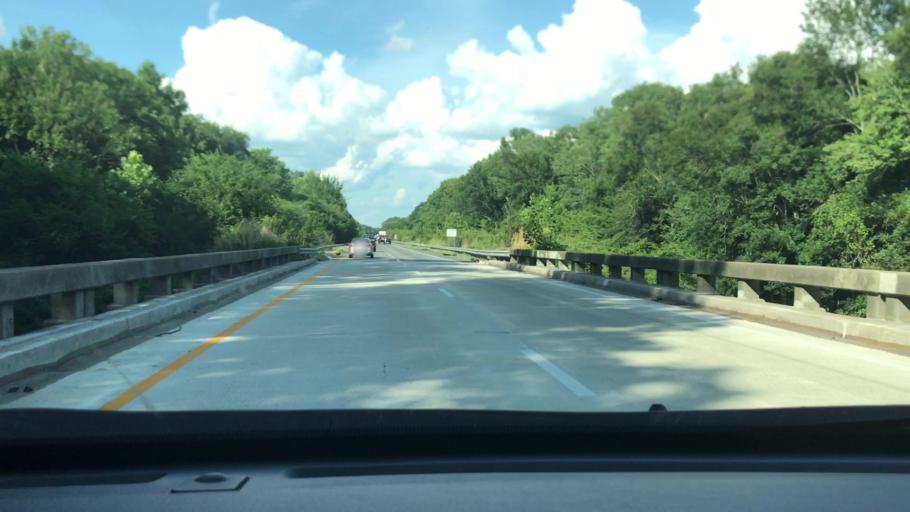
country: US
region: South Carolina
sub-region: Florence County
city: Florence
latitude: 34.3012
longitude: -79.6304
